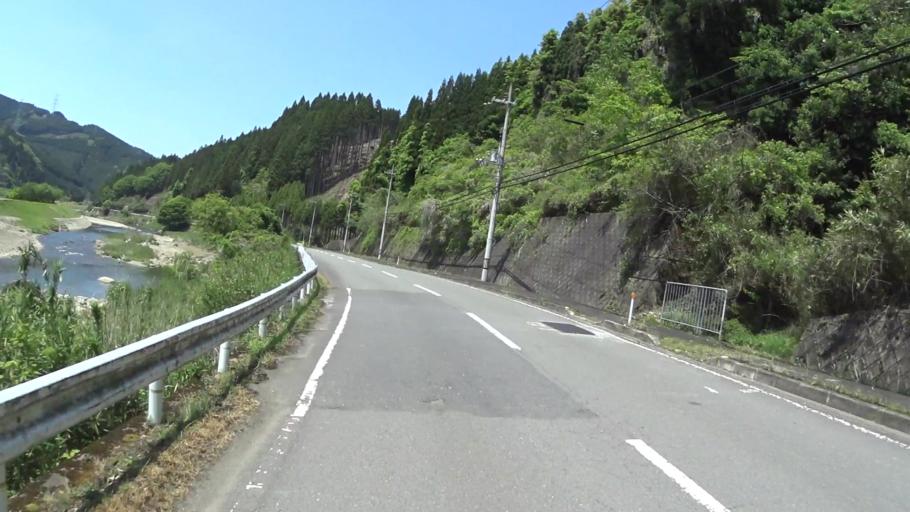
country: JP
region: Kyoto
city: Kameoka
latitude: 35.1385
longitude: 135.6025
